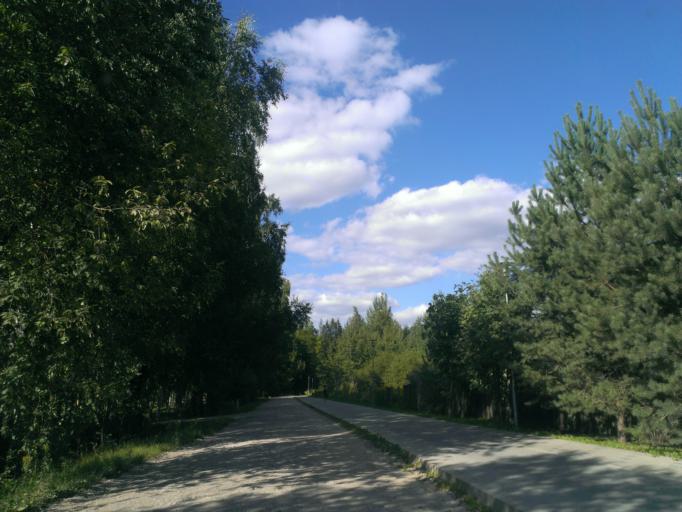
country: LV
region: Sigulda
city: Sigulda
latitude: 57.1683
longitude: 24.8713
